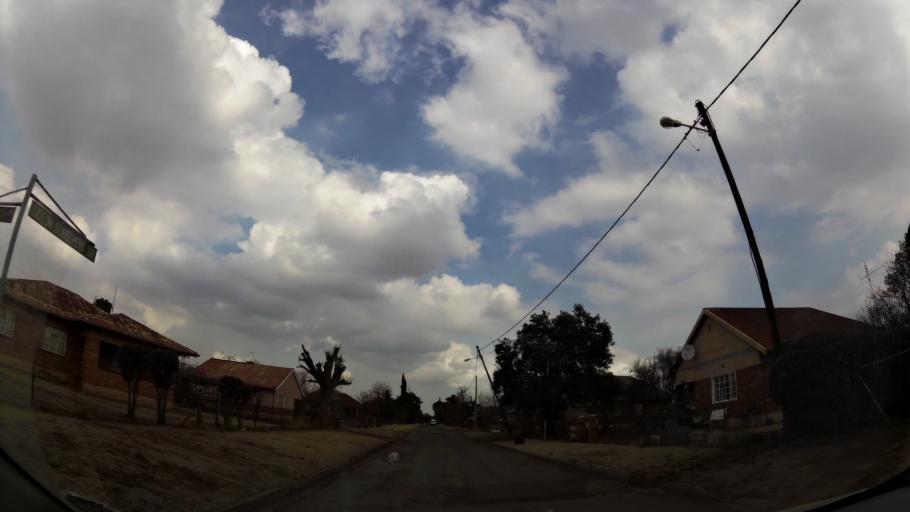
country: ZA
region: Gauteng
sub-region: Sedibeng District Municipality
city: Vereeniging
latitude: -26.6729
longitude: 27.9373
